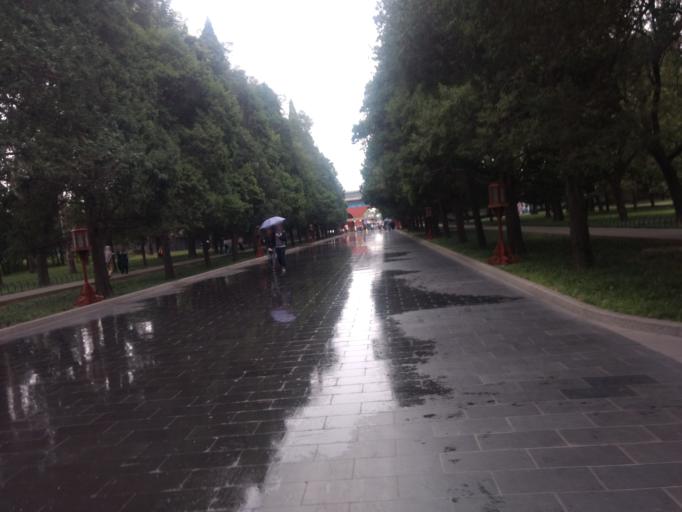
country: CN
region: Beijing
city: Beijing
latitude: 39.8797
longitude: 116.3961
